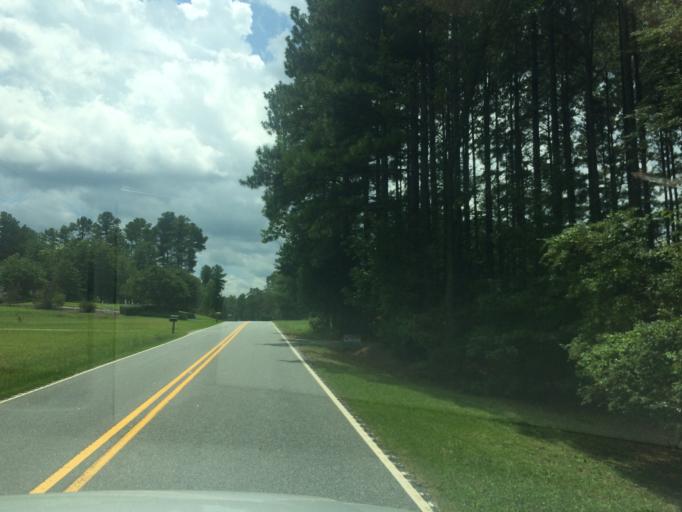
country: US
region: South Carolina
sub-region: Spartanburg County
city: Landrum
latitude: 35.1972
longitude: -82.0505
